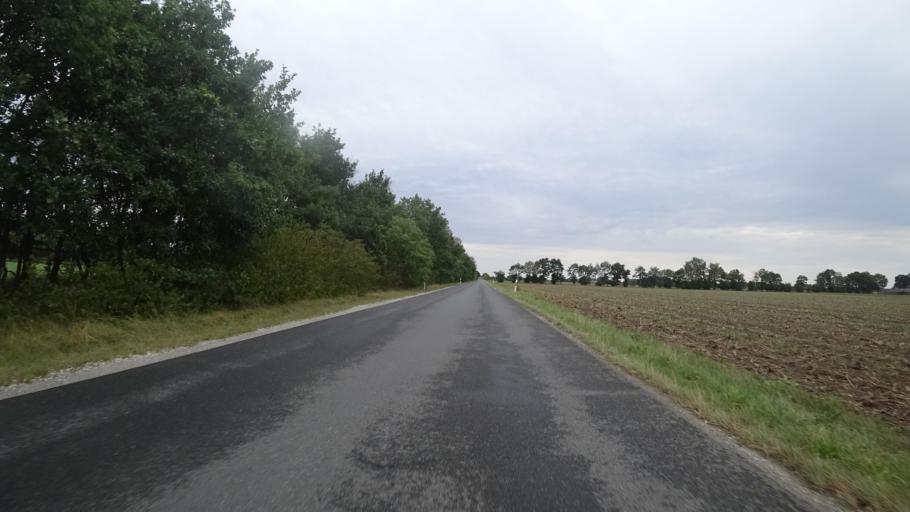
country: DE
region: North Rhine-Westphalia
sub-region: Regierungsbezirk Detmold
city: Rheda-Wiedenbruck
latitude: 51.8855
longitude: 8.2979
